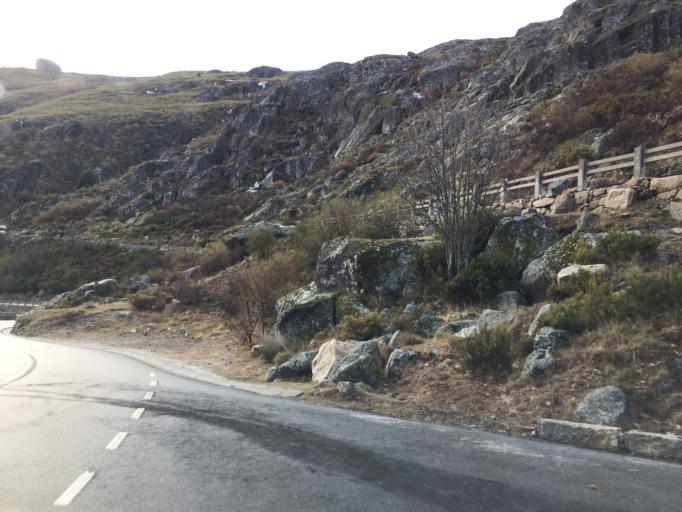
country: PT
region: Guarda
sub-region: Manteigas
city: Manteigas
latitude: 40.3277
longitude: -7.5866
